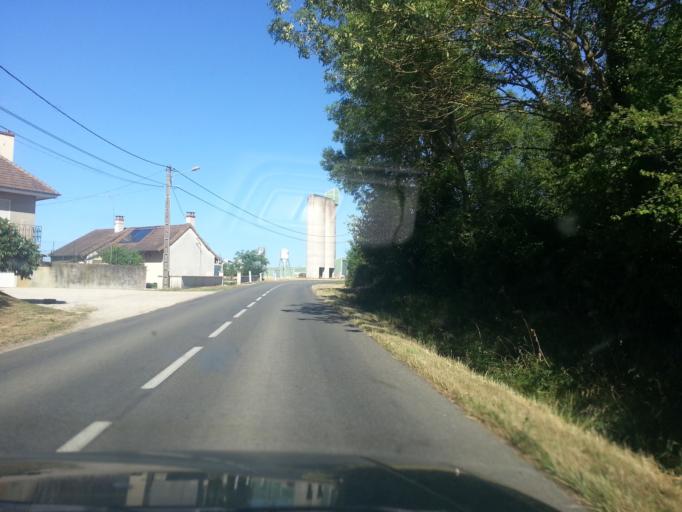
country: FR
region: Bourgogne
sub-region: Departement de Saone-et-Loire
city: Saint-Martin-en-Bresse
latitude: 46.8152
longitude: 5.0649
